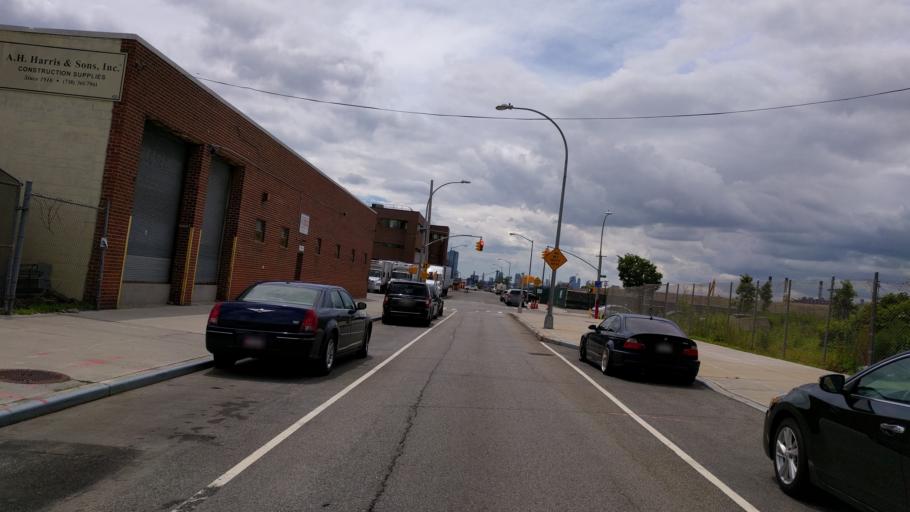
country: US
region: New York
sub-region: Queens County
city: Long Island City
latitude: 40.7414
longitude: -73.9591
